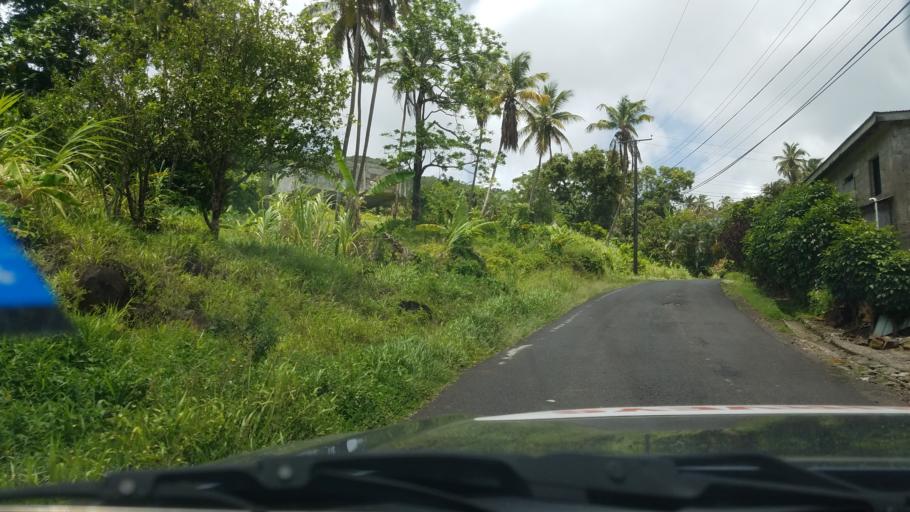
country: LC
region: Castries Quarter
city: Bisee
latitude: 13.9905
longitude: -60.9249
